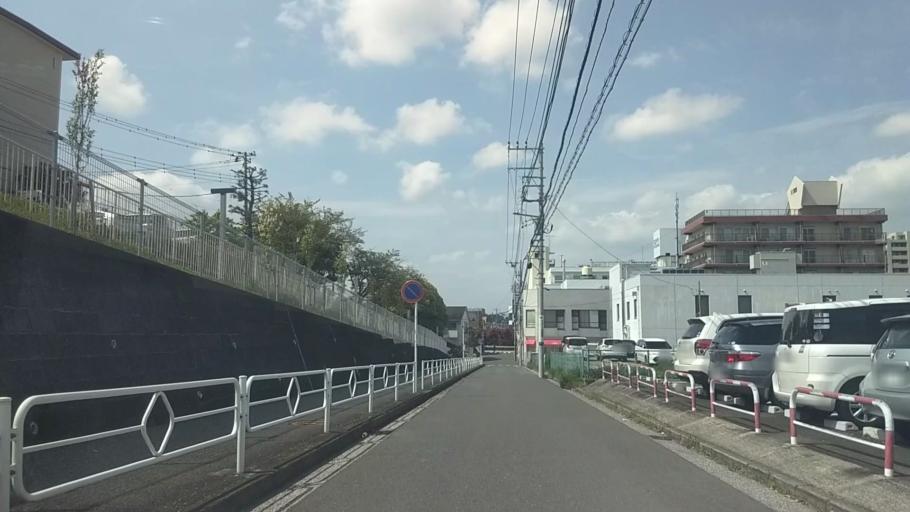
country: JP
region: Kanagawa
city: Kamakura
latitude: 35.3734
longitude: 139.5764
